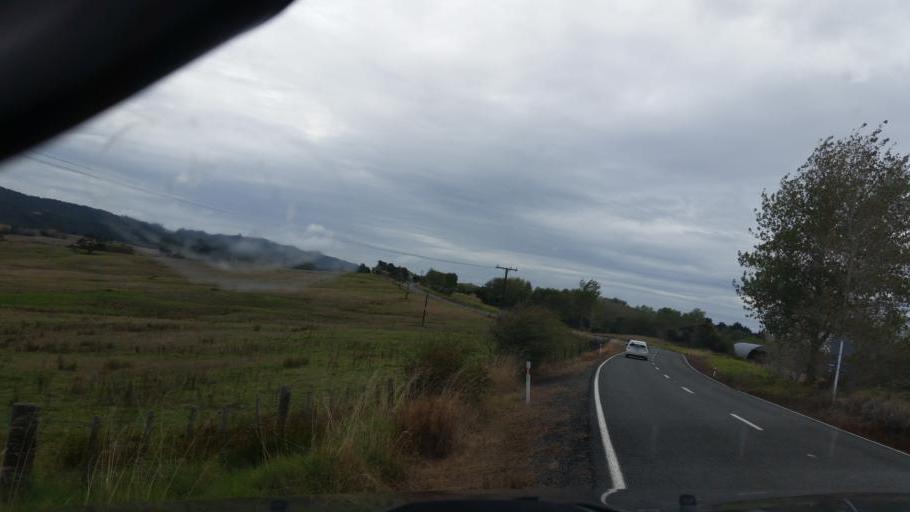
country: NZ
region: Auckland
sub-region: Auckland
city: Wellsford
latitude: -36.1511
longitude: 174.4740
